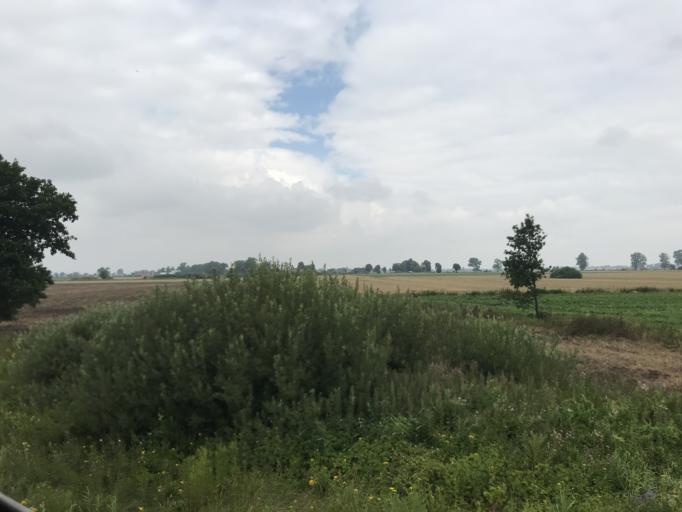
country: PL
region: Pomeranian Voivodeship
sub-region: Powiat malborski
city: Malbork
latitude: 54.0587
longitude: 18.9945
